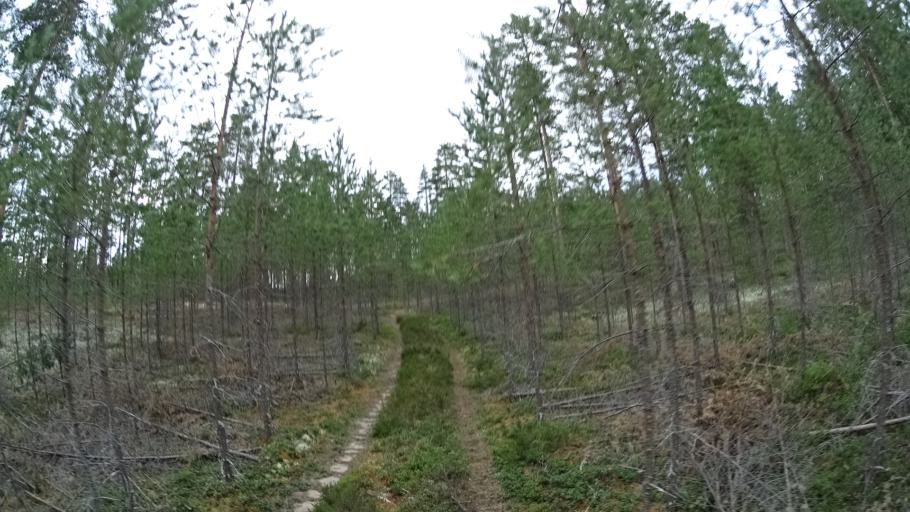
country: FI
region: Satakunta
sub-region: Pohjois-Satakunta
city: Jaemijaervi
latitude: 61.7650
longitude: 22.7604
